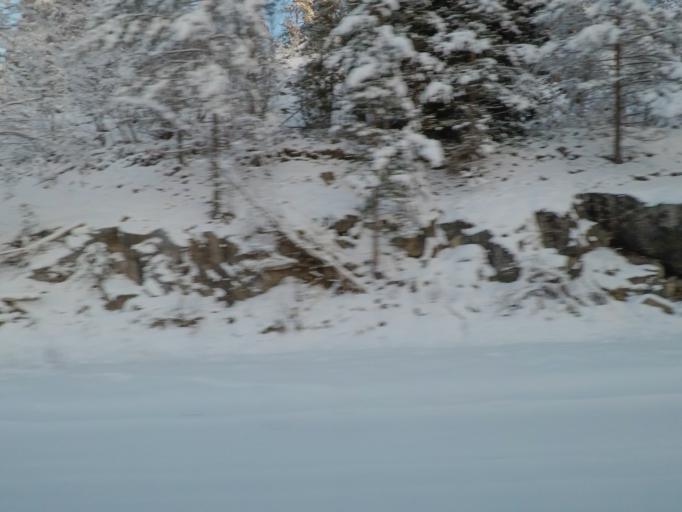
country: FI
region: Uusimaa
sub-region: Helsinki
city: Karjalohja
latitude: 60.2748
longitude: 23.6621
